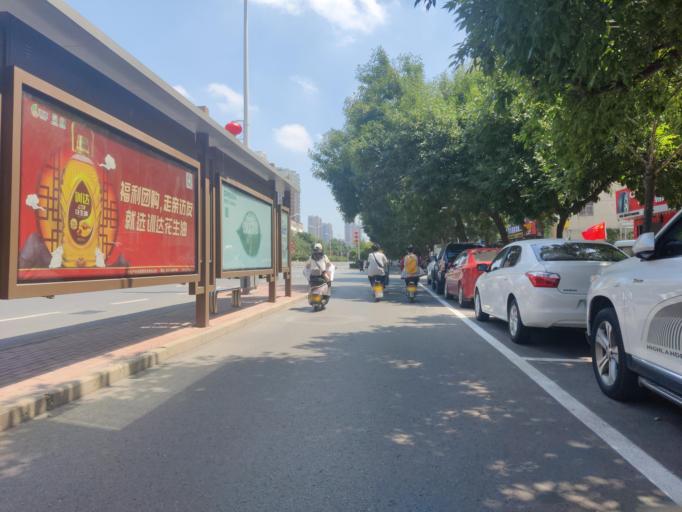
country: CN
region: Henan Sheng
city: Puyang
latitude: 35.7724
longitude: 115.0222
